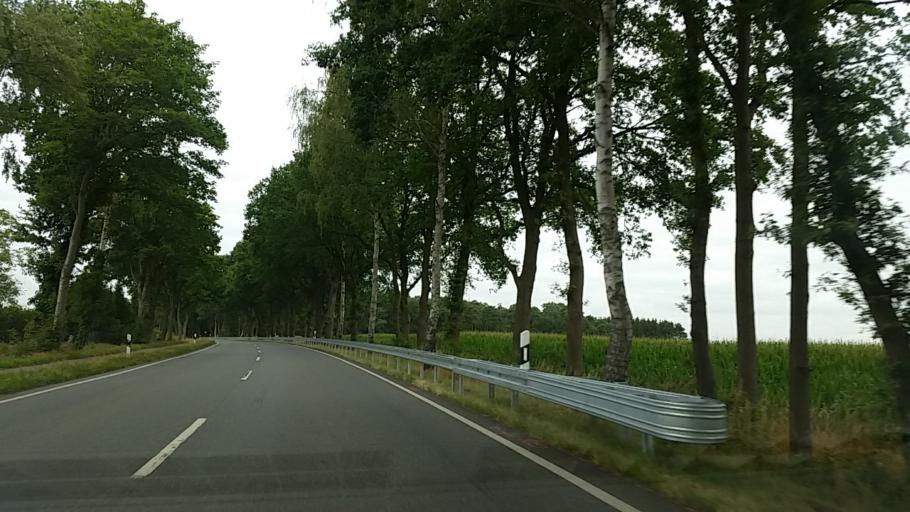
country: DE
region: Lower Saxony
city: Beverstedt
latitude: 53.4307
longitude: 8.8572
